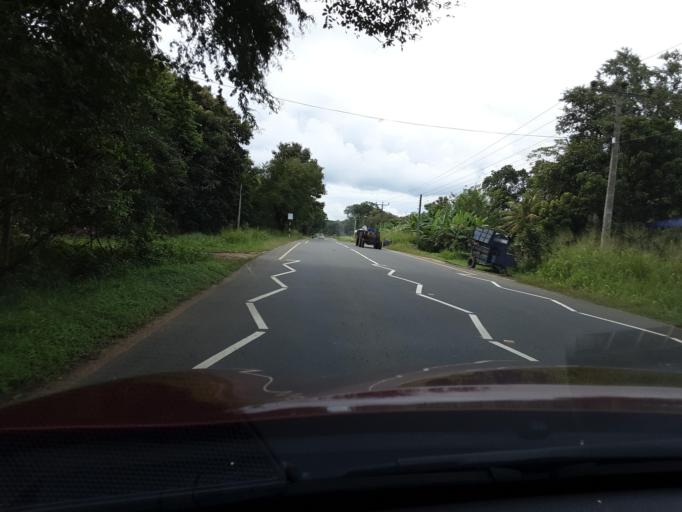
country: LK
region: Uva
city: Badulla
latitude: 7.3939
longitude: 81.1286
